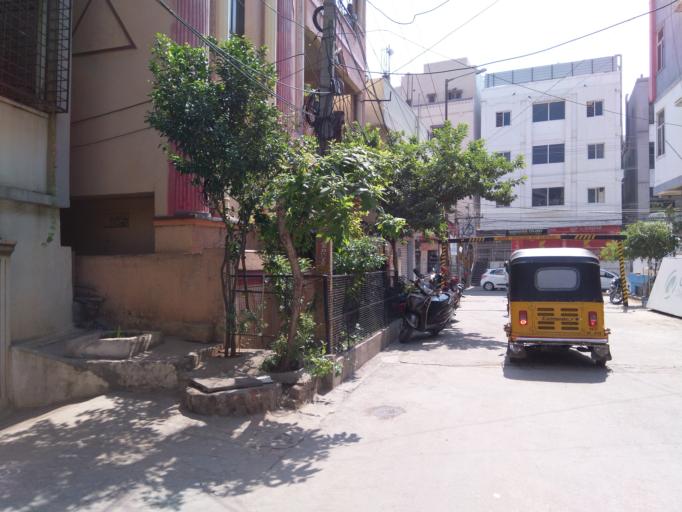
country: IN
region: Telangana
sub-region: Rangareddi
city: Kukatpalli
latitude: 17.4977
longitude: 78.4076
